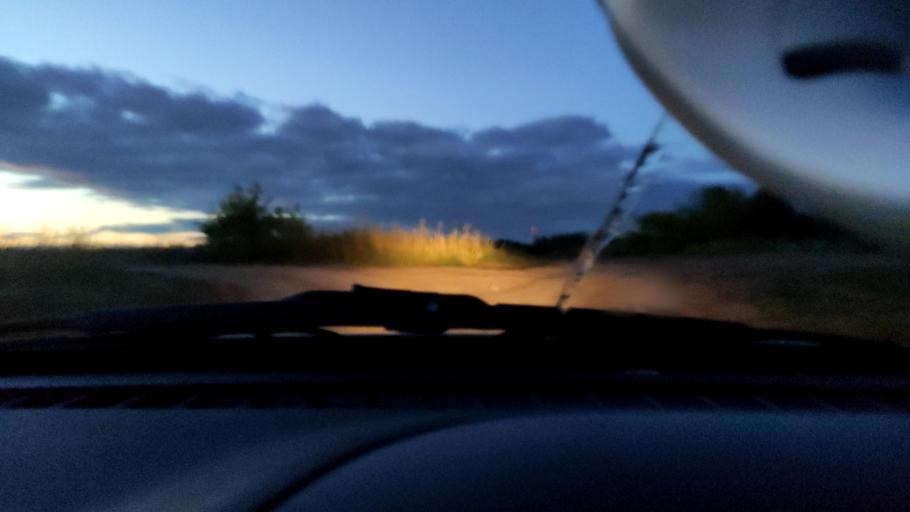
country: RU
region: Perm
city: Froly
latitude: 57.9436
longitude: 56.2528
